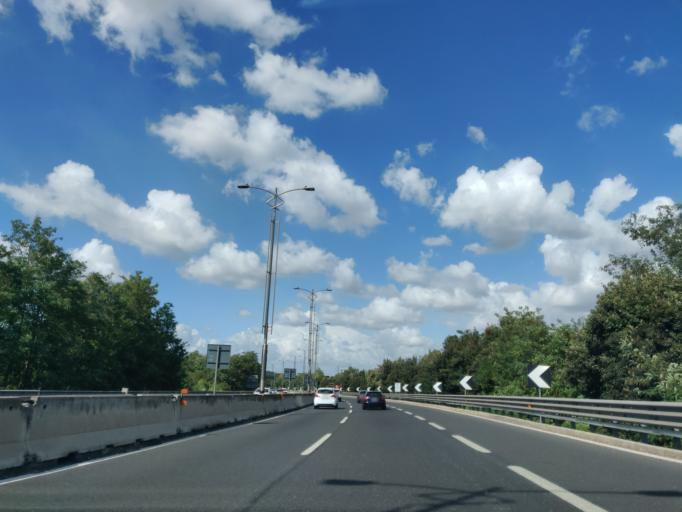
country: IT
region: Latium
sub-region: Citta metropolitana di Roma Capitale
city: Vitinia
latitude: 41.8224
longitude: 12.4181
